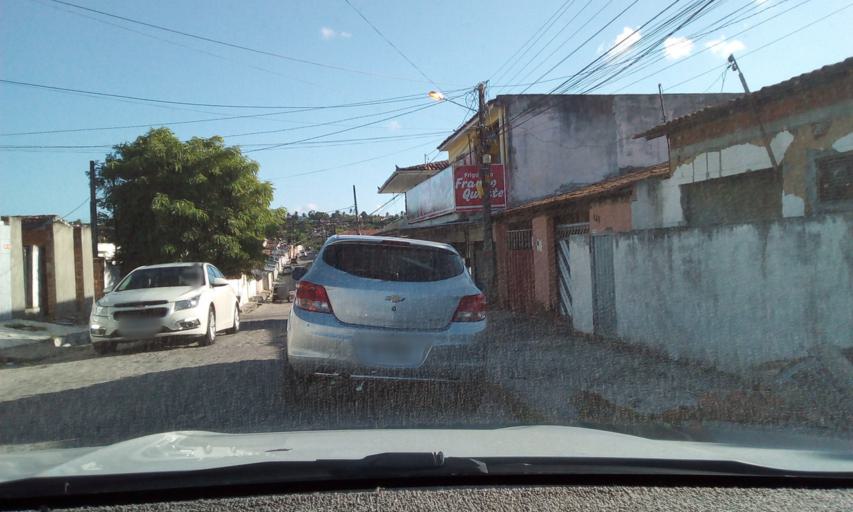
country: BR
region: Paraiba
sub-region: Bayeux
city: Bayeux
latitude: -7.1270
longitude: -34.9169
